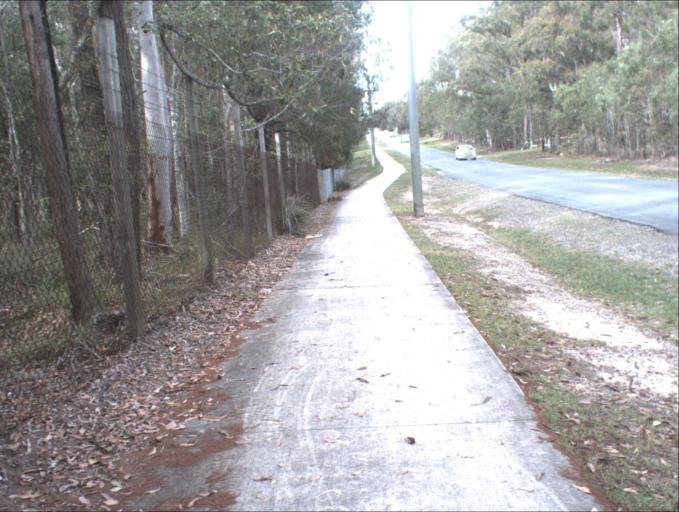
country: AU
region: Queensland
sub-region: Logan
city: Logan Reserve
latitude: -27.6978
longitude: 153.0770
